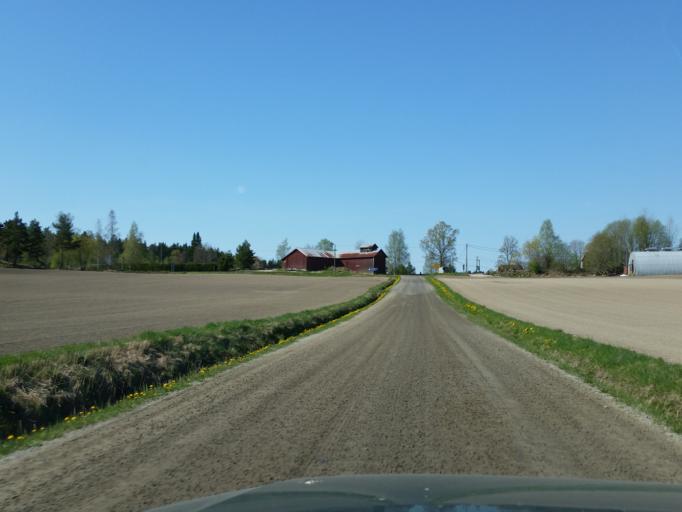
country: FI
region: Uusimaa
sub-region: Helsinki
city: Karjalohja
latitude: 60.1451
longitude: 23.7740
